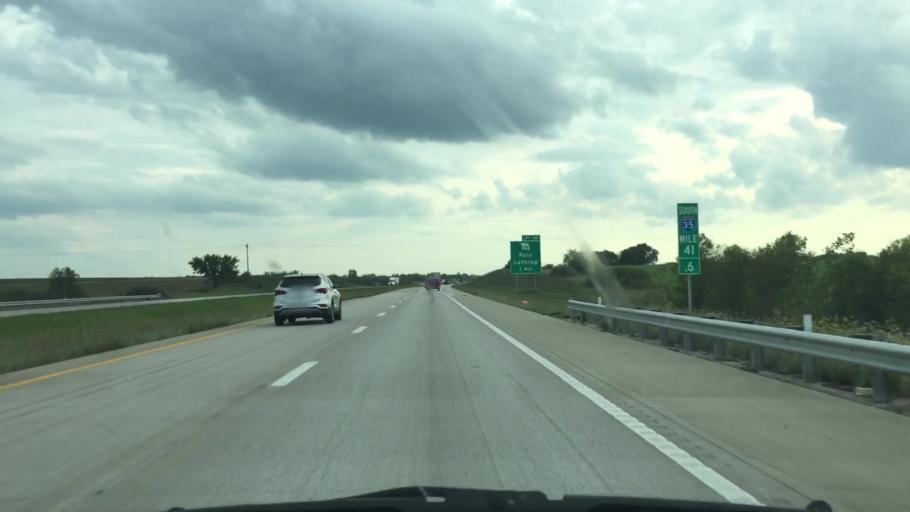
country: US
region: Missouri
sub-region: Clinton County
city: Lathrop
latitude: 39.5743
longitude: -94.2615
